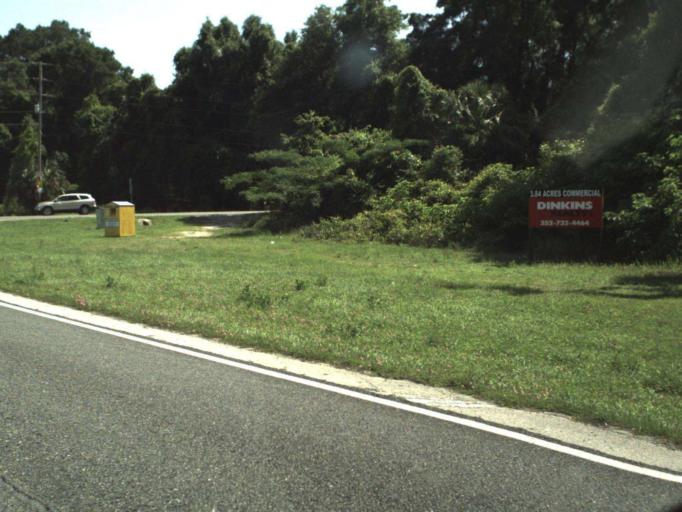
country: US
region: Florida
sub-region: Marion County
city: Belleview
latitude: 29.1070
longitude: -82.0921
